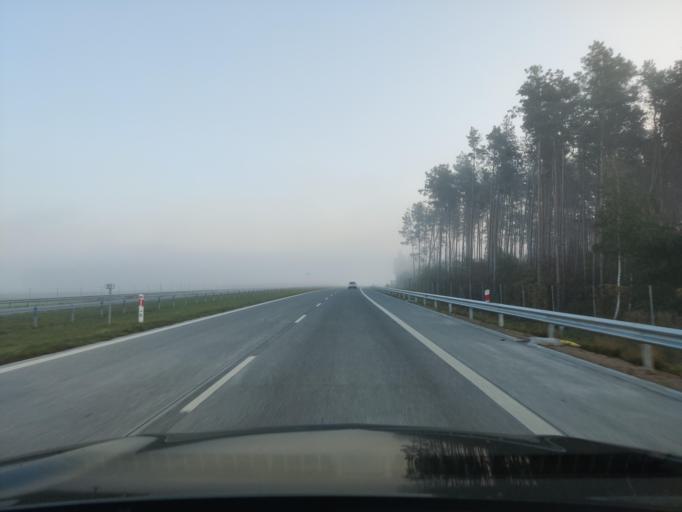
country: PL
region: Masovian Voivodeship
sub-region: Powiat mlawski
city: Strzegowo
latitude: 52.9530
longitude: 20.3028
